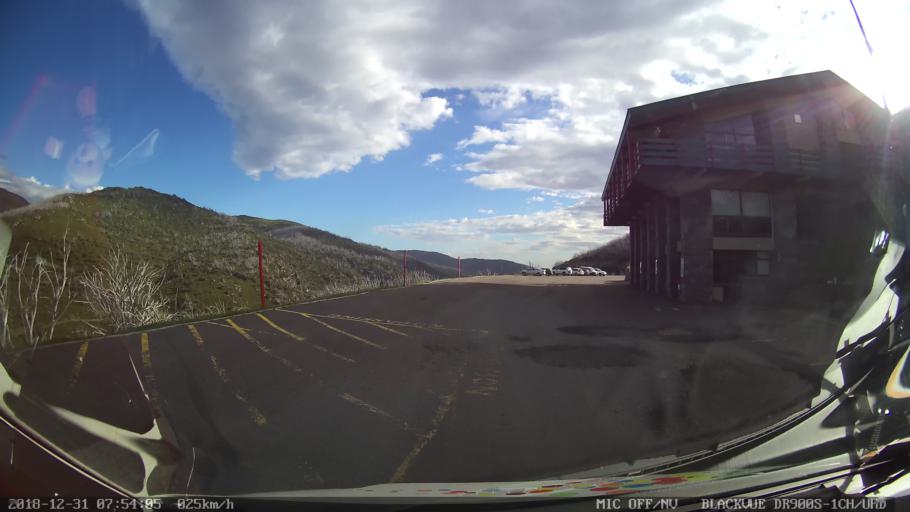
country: AU
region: New South Wales
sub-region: Snowy River
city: Jindabyne
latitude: -36.3782
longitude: 148.3751
